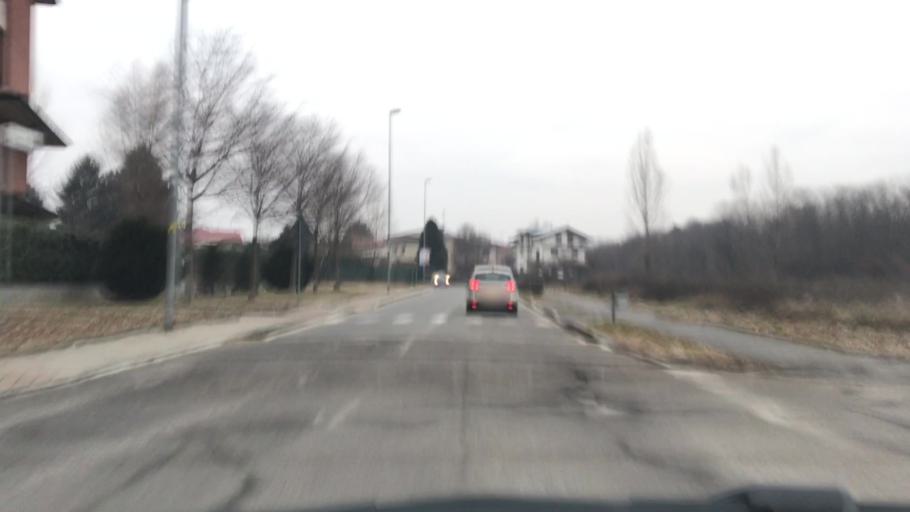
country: IT
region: Lombardy
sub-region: Provincia di Monza e Brianza
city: Seveso
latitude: 45.6462
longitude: 9.1467
